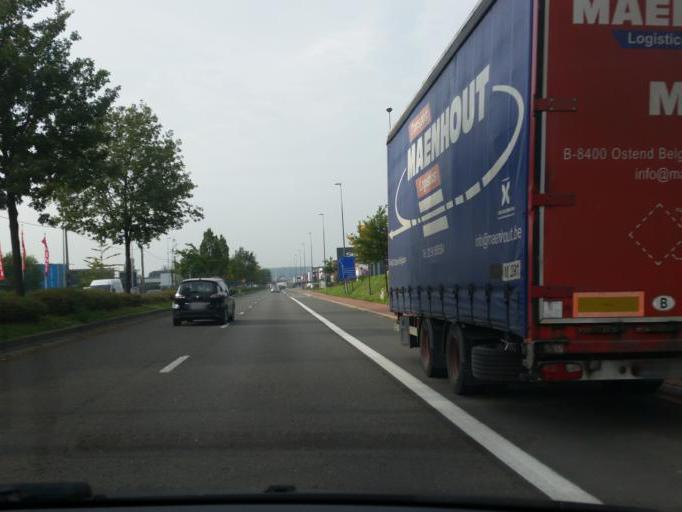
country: BE
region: Flanders
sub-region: Provincie Vlaams-Brabant
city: Sint-Pieters-Leeuw
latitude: 50.7686
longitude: 4.2580
